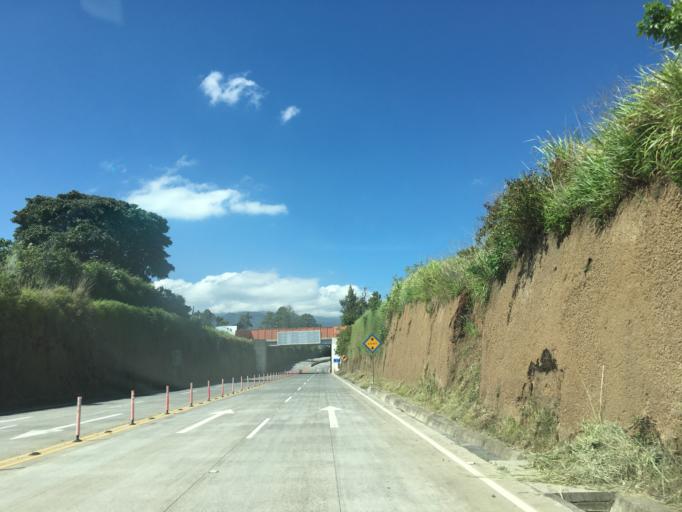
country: GT
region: Guatemala
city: Amatitlan
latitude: 14.4908
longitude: -90.5855
